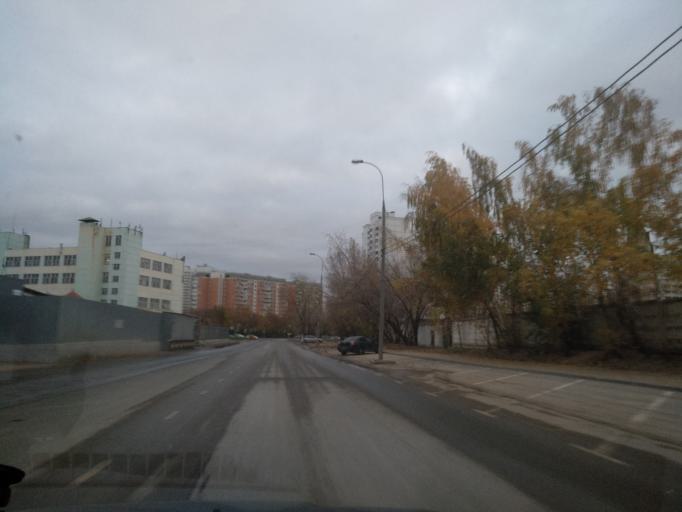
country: RU
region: Moscow
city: Kozeyevo
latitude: 55.8845
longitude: 37.6384
